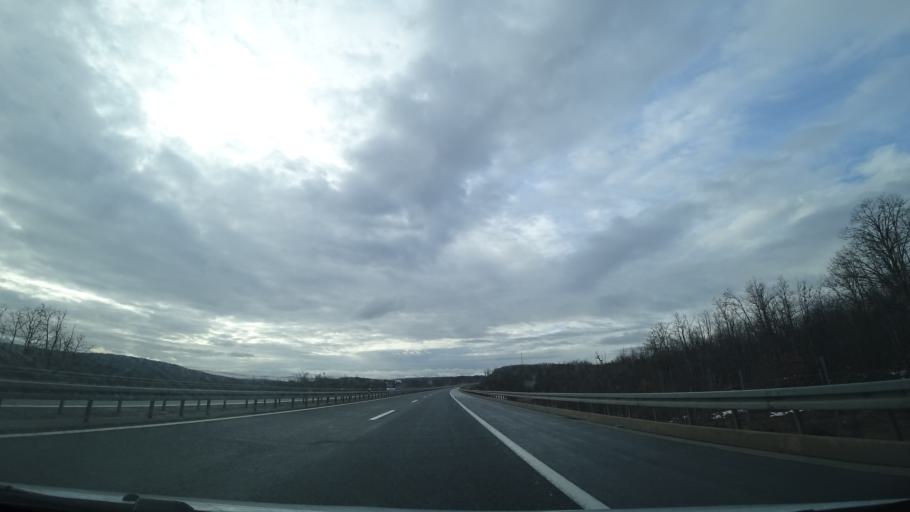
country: HR
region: Licko-Senjska
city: Gospic
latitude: 44.7296
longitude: 15.3841
